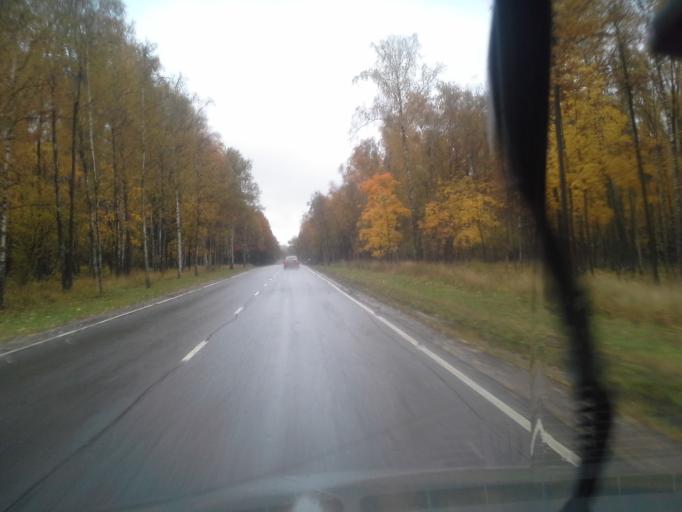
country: RU
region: Moskovskaya
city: Odintsovo
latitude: 55.6943
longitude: 37.2331
